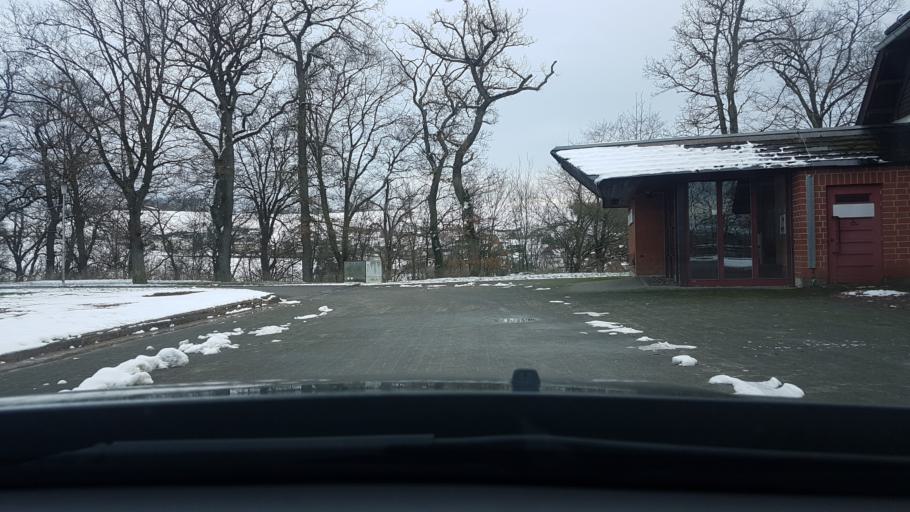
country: DE
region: North Rhine-Westphalia
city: Marsberg
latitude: 51.3629
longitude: 8.8073
